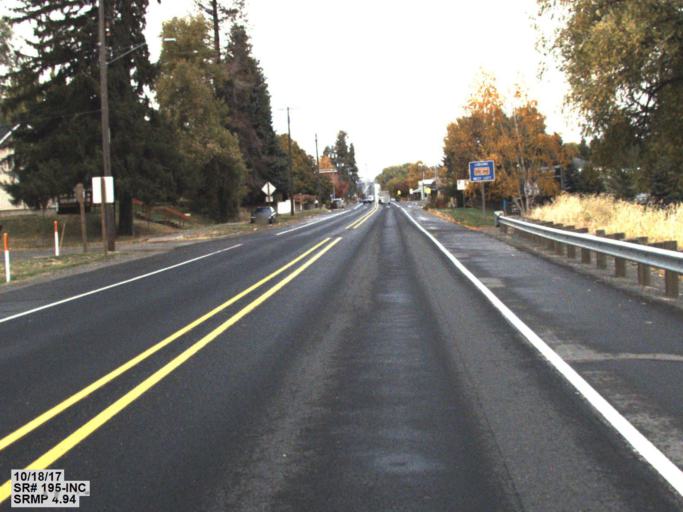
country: US
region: Washington
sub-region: Asotin County
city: Clarkston
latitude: 46.5355
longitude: -117.0864
